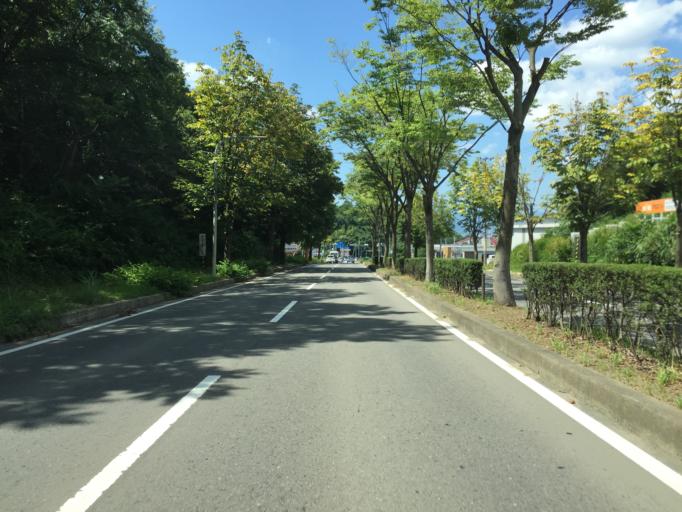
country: JP
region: Fukushima
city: Fukushima-shi
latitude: 37.7091
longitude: 140.4689
